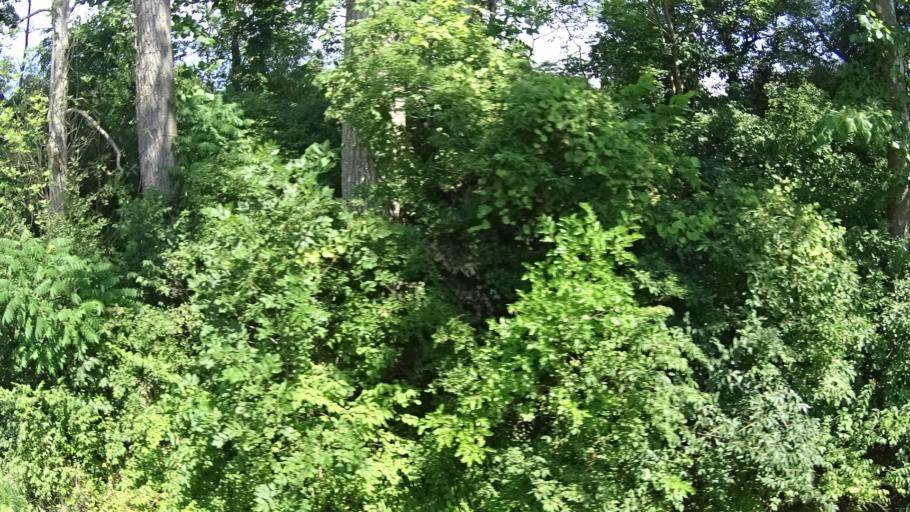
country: US
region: Ohio
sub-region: Erie County
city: Sandusky
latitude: 41.4270
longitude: -82.7790
